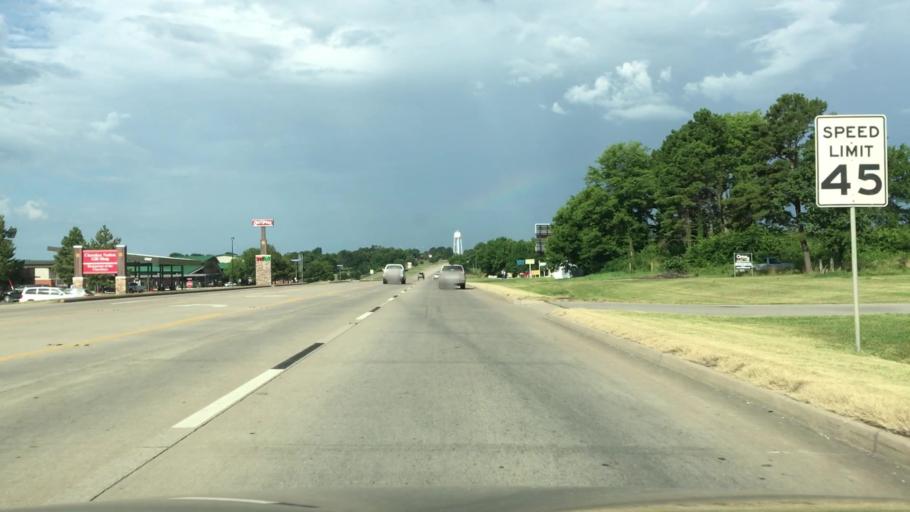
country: US
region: Oklahoma
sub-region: Cherokee County
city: Park Hill
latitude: 35.8544
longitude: -94.9880
